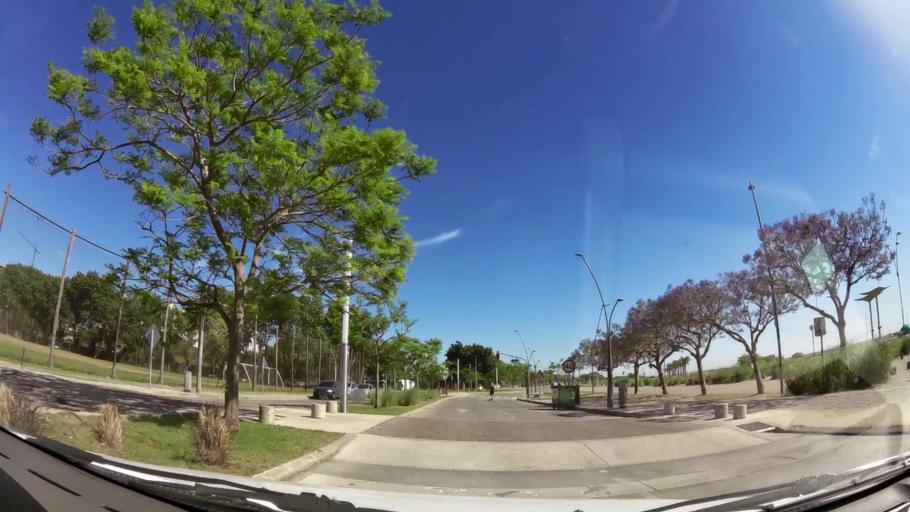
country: AR
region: Buenos Aires
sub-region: Partido de Vicente Lopez
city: Olivos
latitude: -34.5249
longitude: -58.4681
